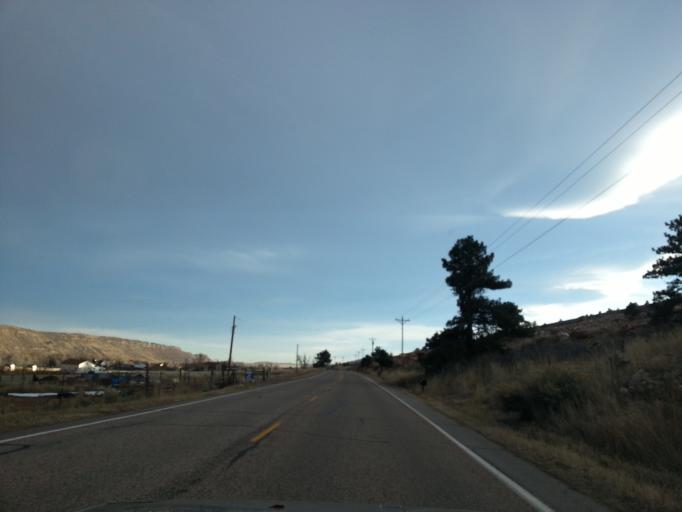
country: US
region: Colorado
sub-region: Larimer County
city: Loveland
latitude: 40.4767
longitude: -105.2142
